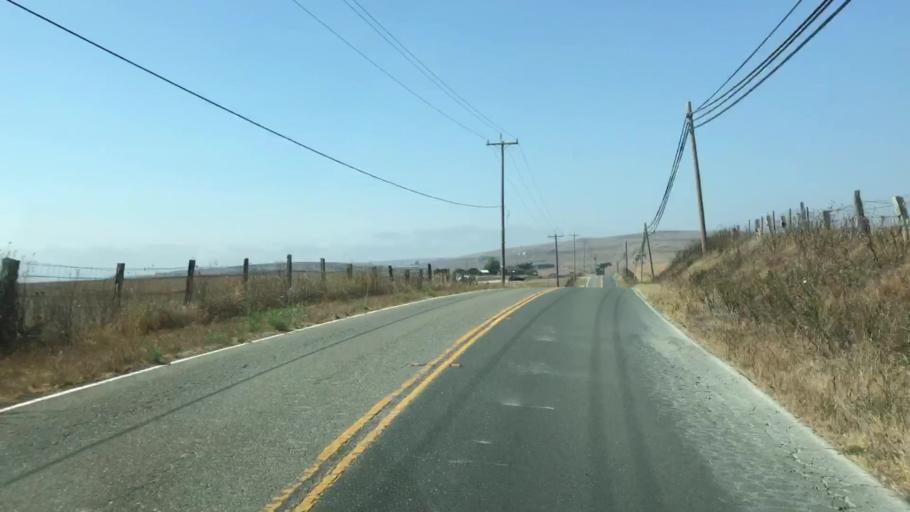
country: US
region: California
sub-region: Marin County
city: Inverness
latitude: 38.0852
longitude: -122.8118
